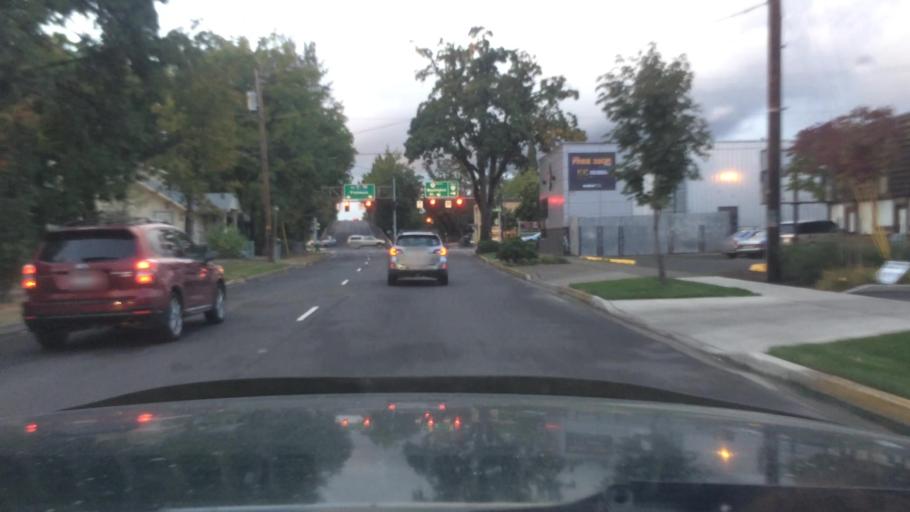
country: US
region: Oregon
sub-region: Lane County
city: Eugene
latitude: 44.0511
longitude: -123.1003
